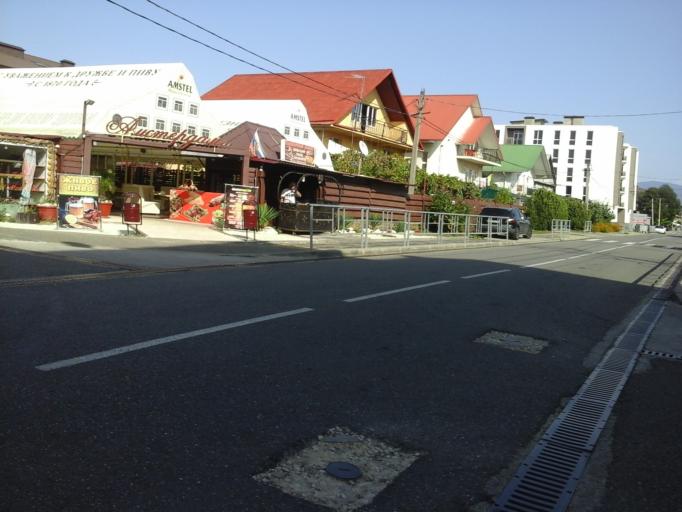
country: RU
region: Krasnodarskiy
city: Adler
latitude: 43.4118
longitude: 39.9577
